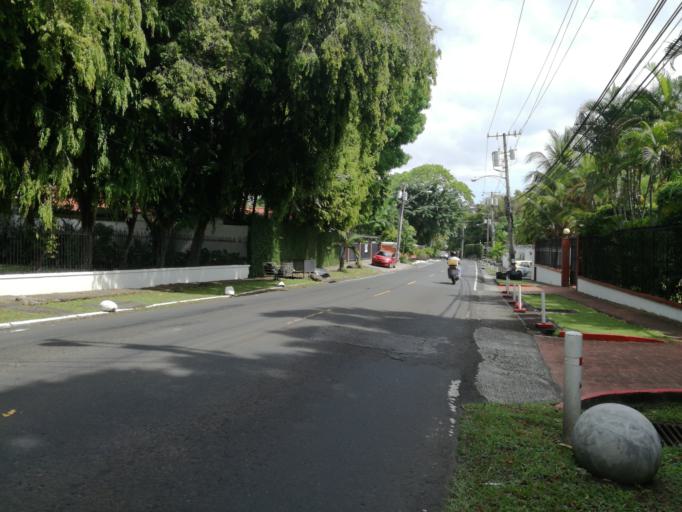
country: PA
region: Panama
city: Panama
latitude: 8.9998
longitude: -79.5033
